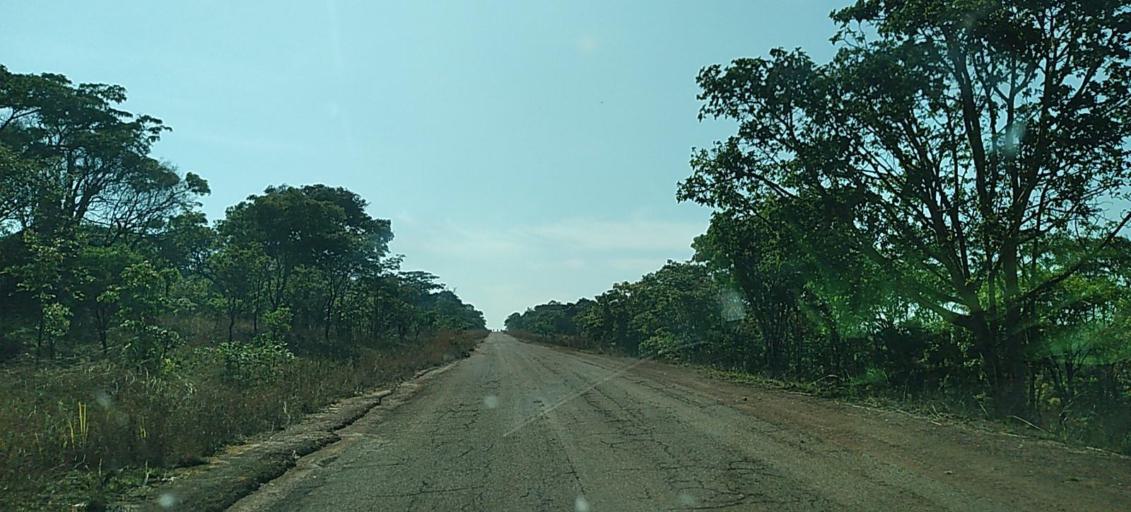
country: ZM
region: North-Western
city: Mwinilunga
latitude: -11.7869
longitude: 25.0494
